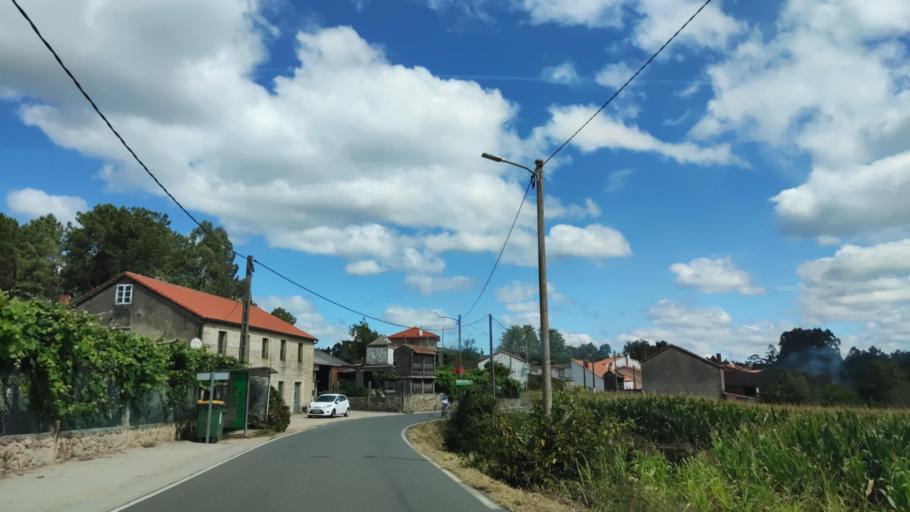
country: ES
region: Galicia
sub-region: Provincia da Coruna
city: Rois
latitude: 42.7794
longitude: -8.6694
